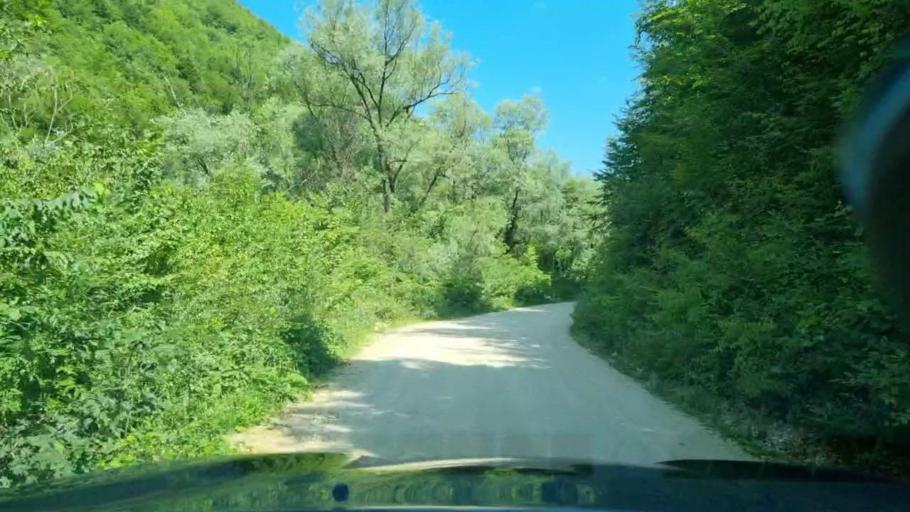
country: BA
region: Federation of Bosnia and Herzegovina
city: Peci
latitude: 44.5958
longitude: 16.8248
